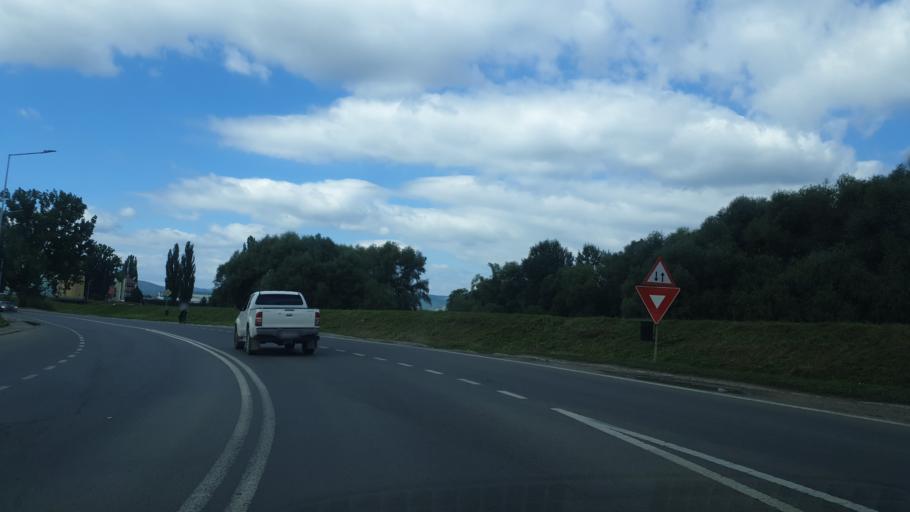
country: RO
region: Covasna
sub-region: Municipiul Sfantu Gheorghe
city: Sfantu-Gheorghe
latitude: 45.8645
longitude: 25.8035
